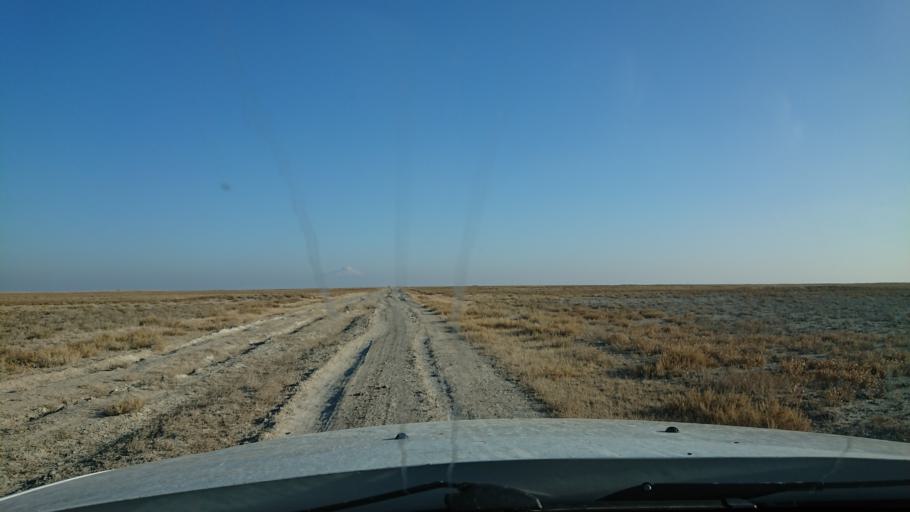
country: TR
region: Aksaray
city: Eskil
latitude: 38.4060
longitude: 33.5714
